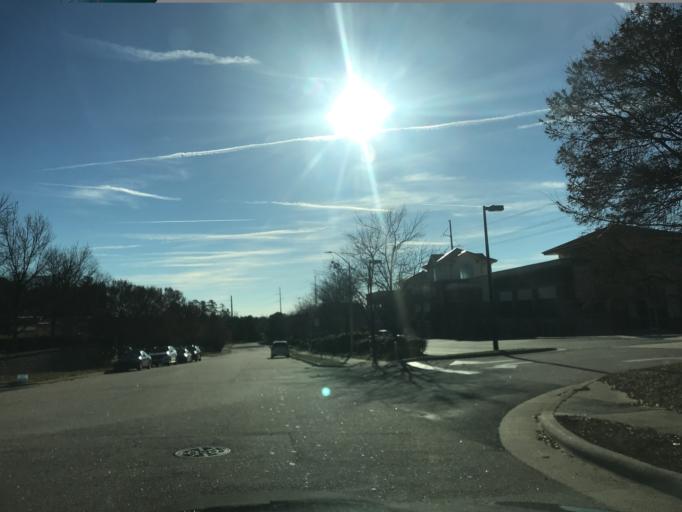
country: US
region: North Carolina
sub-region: Wake County
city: West Raleigh
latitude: 35.8985
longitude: -78.6081
